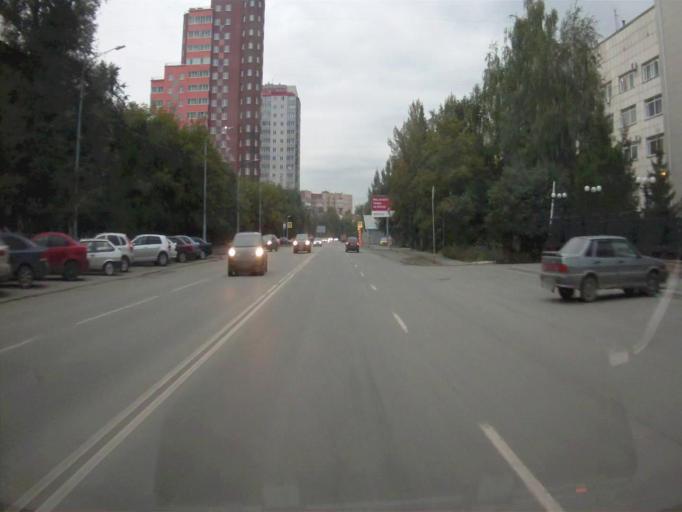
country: RU
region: Chelyabinsk
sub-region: Gorod Chelyabinsk
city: Chelyabinsk
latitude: 55.1503
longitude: 61.3985
